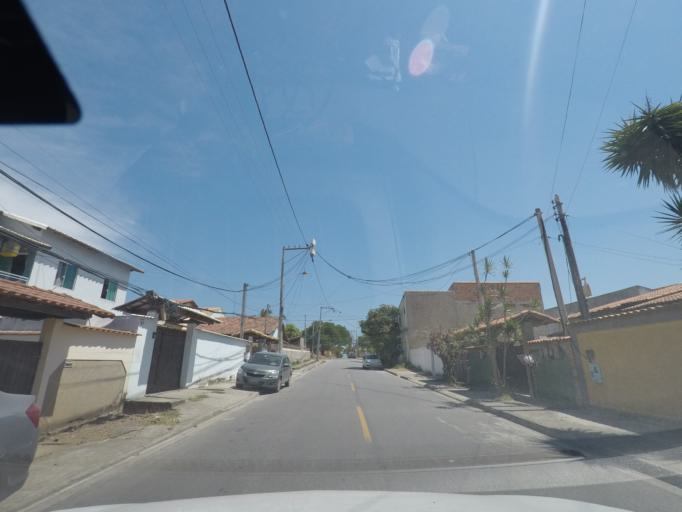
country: BR
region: Rio de Janeiro
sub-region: Marica
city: Marica
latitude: -22.9639
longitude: -42.9567
